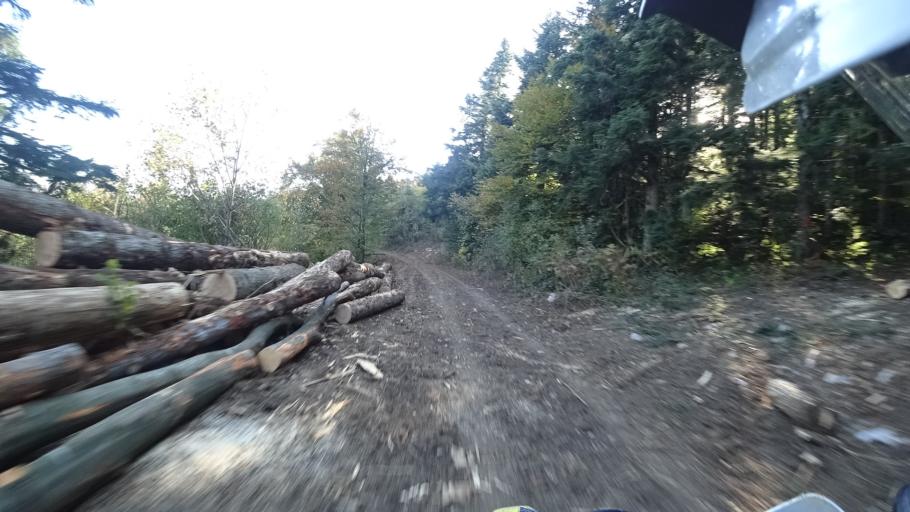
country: HR
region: Karlovacka
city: Plaski
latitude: 45.0245
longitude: 15.3903
